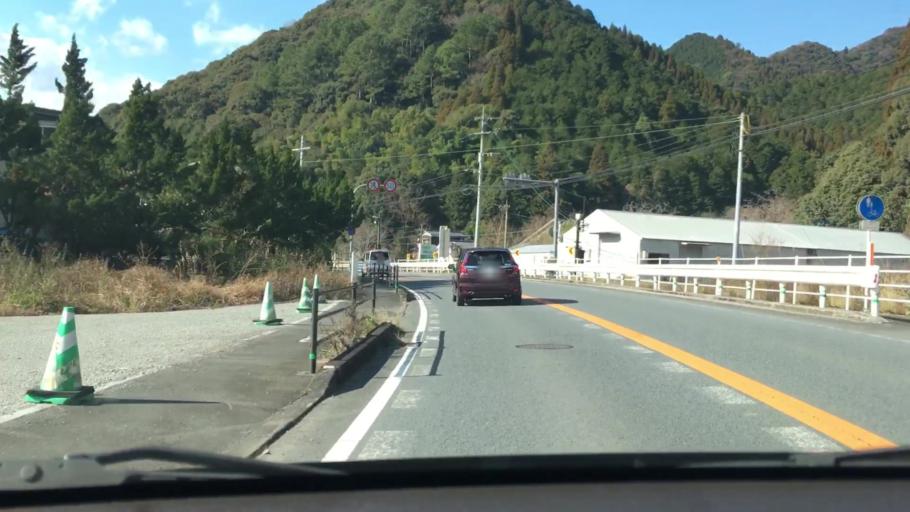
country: JP
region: Oita
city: Saiki
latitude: 32.9861
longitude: 131.8464
